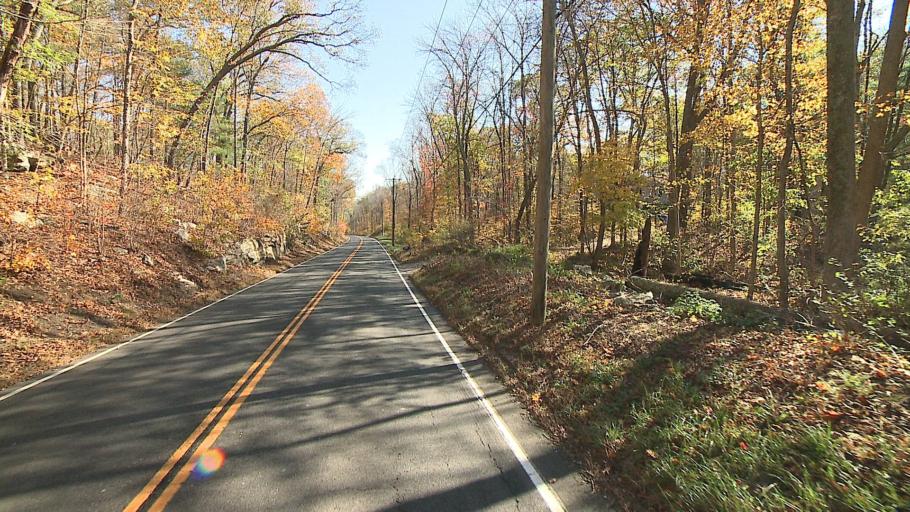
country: US
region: Connecticut
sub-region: Tolland County
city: Coventry Lake
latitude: 41.7982
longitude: -72.3267
